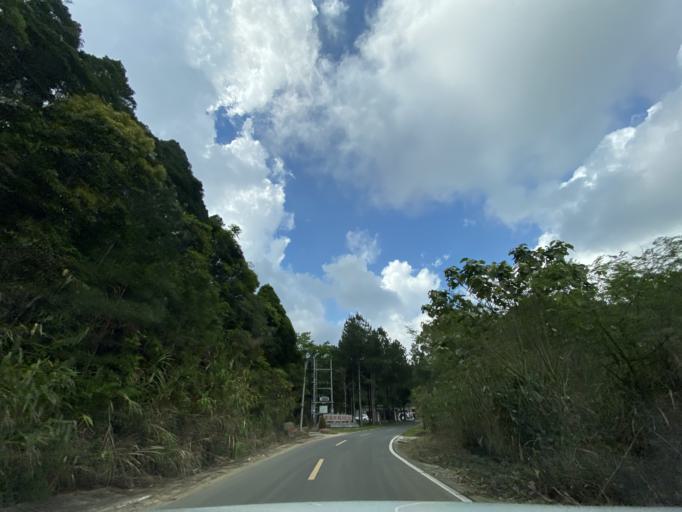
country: CN
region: Hainan
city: Diaoluoshan
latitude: 18.7239
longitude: 109.8689
